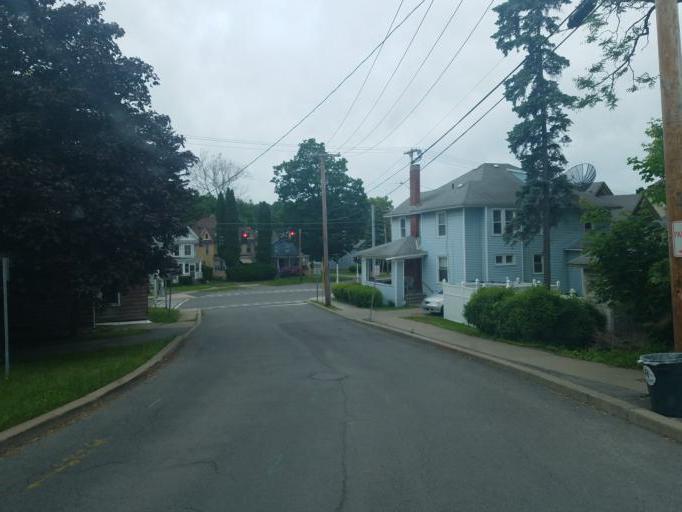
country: US
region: New York
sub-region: Herkimer County
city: Ilion
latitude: 43.0094
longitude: -75.0401
